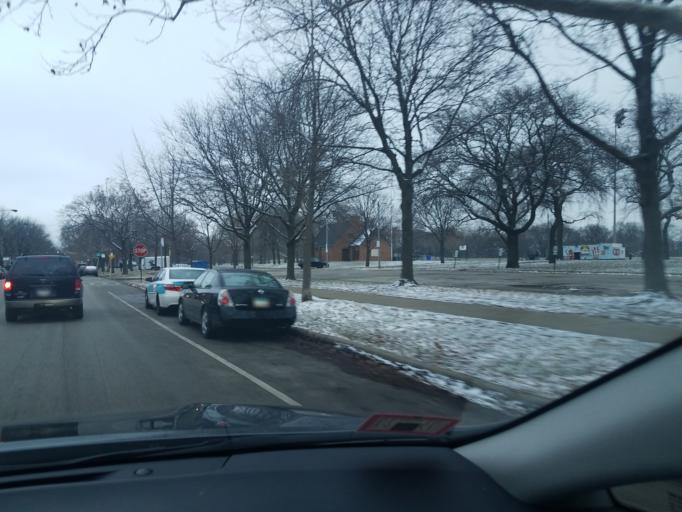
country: US
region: Illinois
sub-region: Cook County
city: Lincolnwood
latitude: 41.9571
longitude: -87.6983
